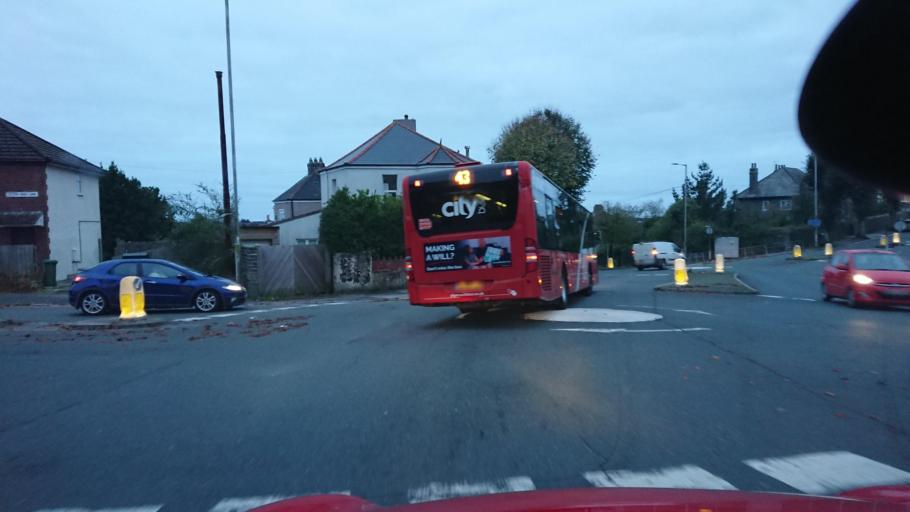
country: GB
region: England
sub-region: Cornwall
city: Torpoint
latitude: 50.4072
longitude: -4.1853
